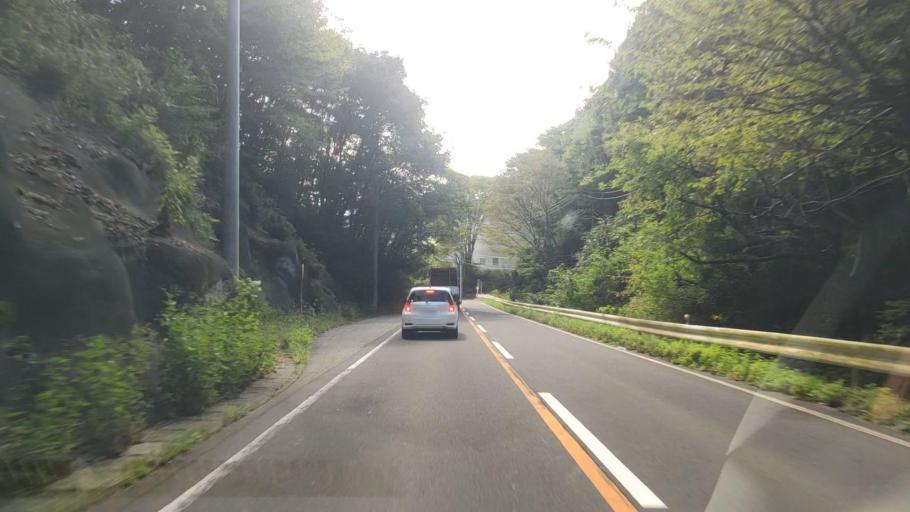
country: JP
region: Gunma
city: Numata
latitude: 36.6289
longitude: 139.0122
